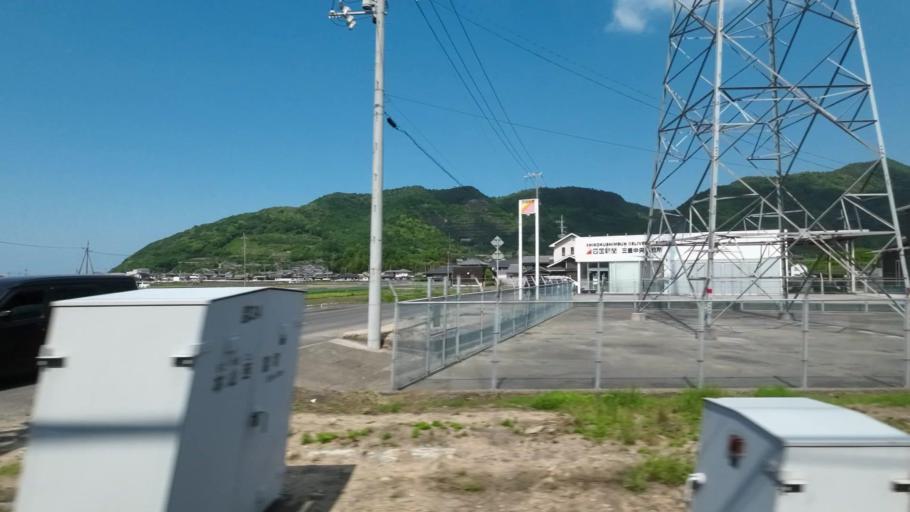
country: JP
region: Kagawa
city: Kan'onjicho
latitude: 34.1449
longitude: 133.6860
